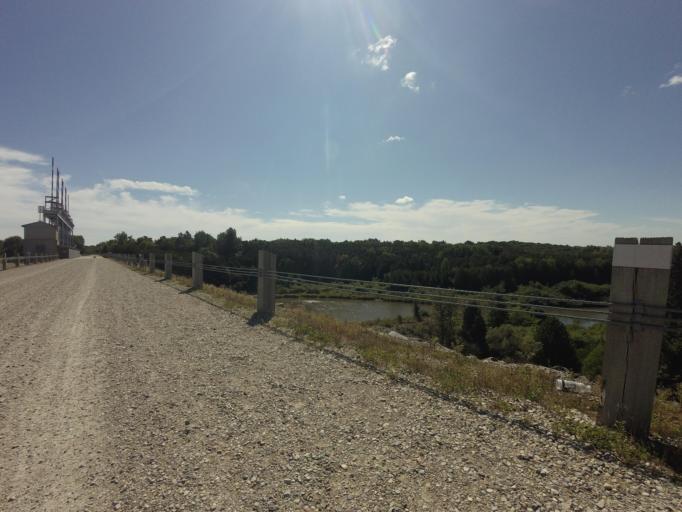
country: CA
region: Ontario
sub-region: Wellington County
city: Guelph
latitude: 43.7346
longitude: -80.3382
